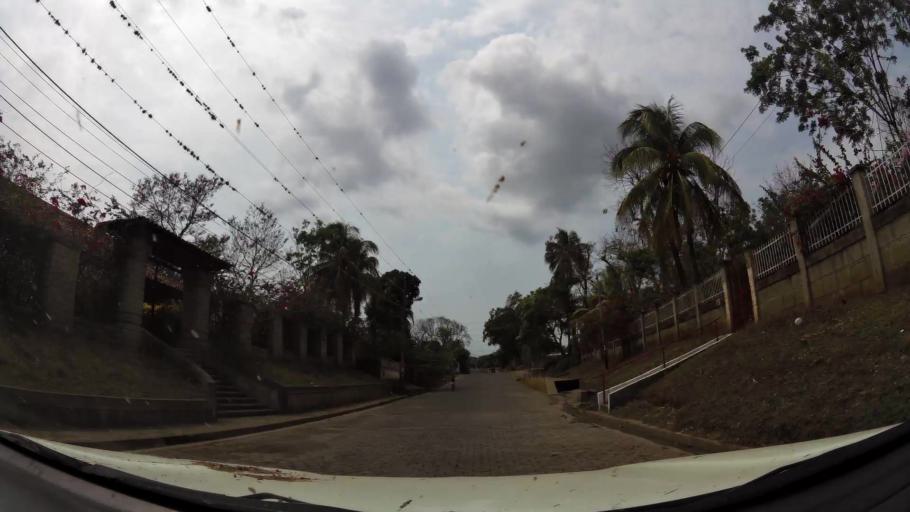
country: NI
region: Granada
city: Diriomo
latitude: 11.8794
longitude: -86.0530
